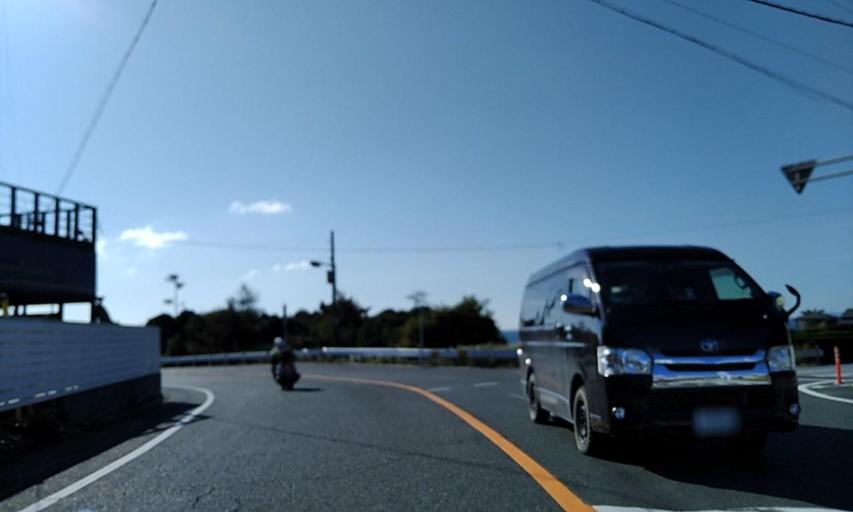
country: JP
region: Aichi
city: Toyohama
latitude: 34.5822
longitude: 137.0228
